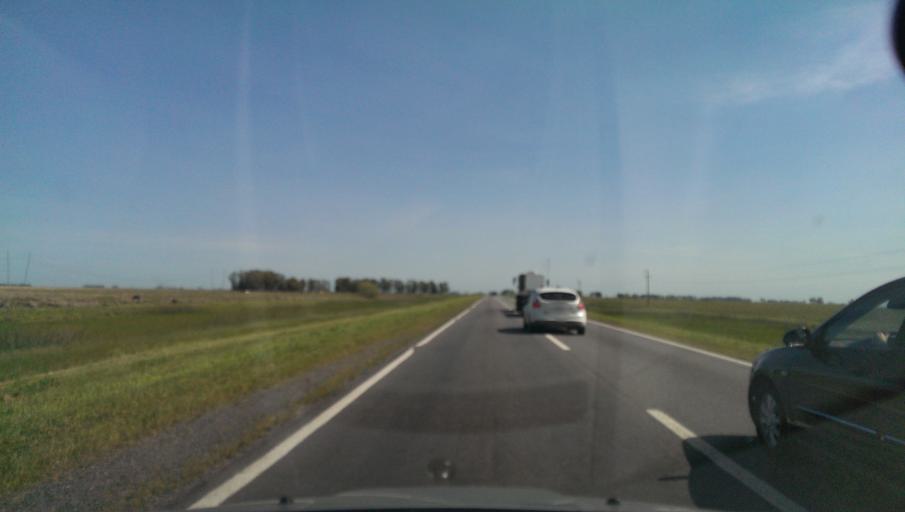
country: AR
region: Buenos Aires
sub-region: Partido de Azul
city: Azul
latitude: -36.5971
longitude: -59.6615
